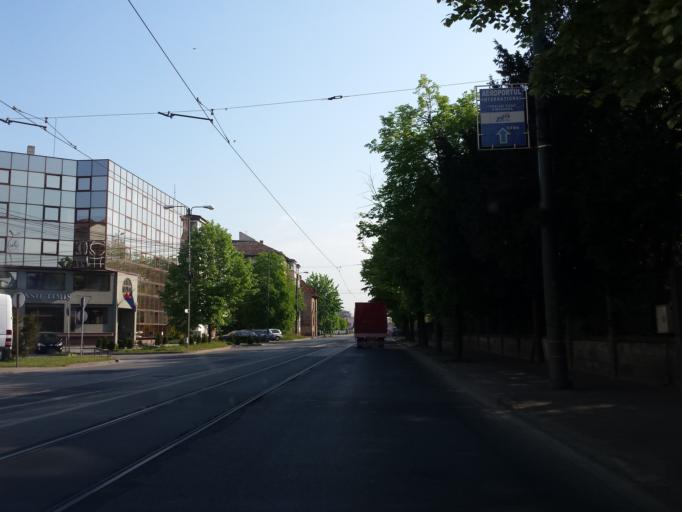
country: RO
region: Timis
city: Timisoara
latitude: 45.7576
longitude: 21.2563
